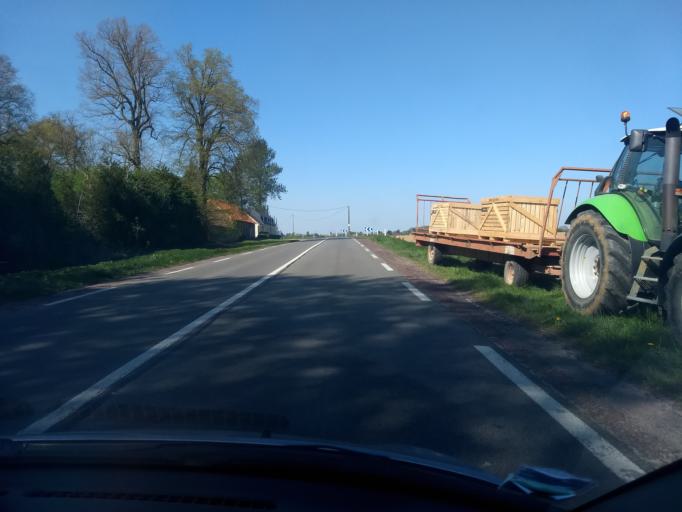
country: FR
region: Picardie
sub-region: Departement de la Somme
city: Villers-Bocage
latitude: 49.9827
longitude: 2.3164
